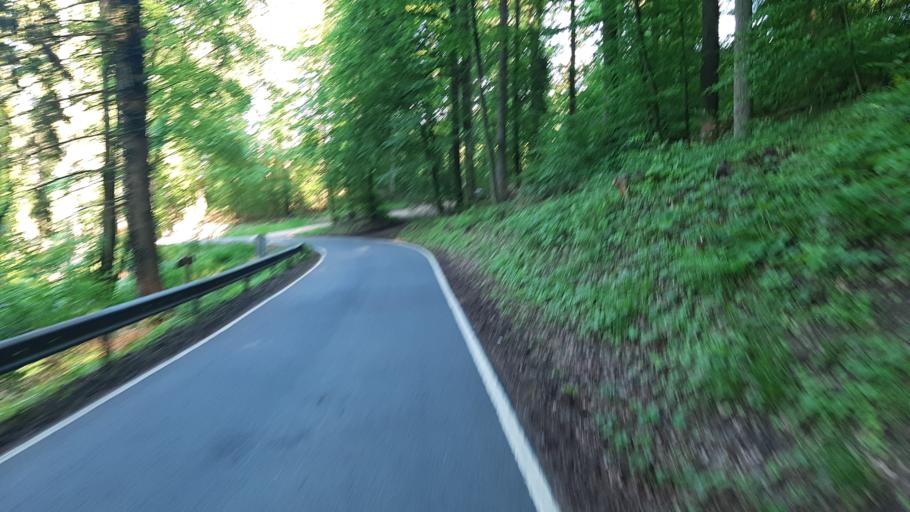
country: DE
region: Rheinland-Pfalz
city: Trierweiler
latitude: 49.7393
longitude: 6.5859
